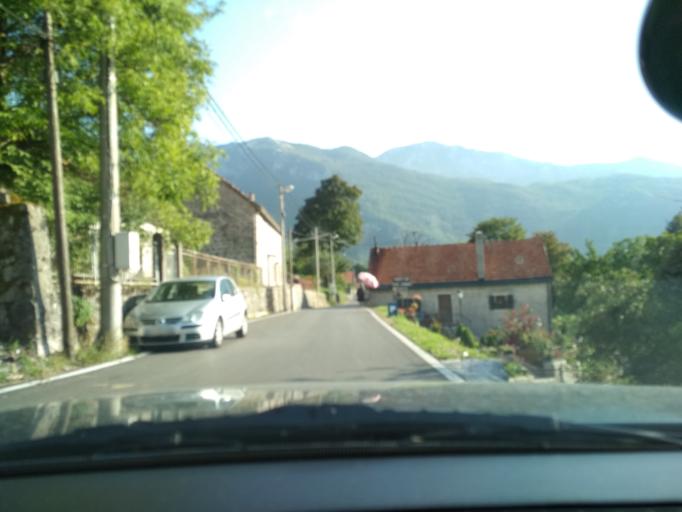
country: ME
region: Kotor
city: Kotor
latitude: 42.4341
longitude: 18.8294
